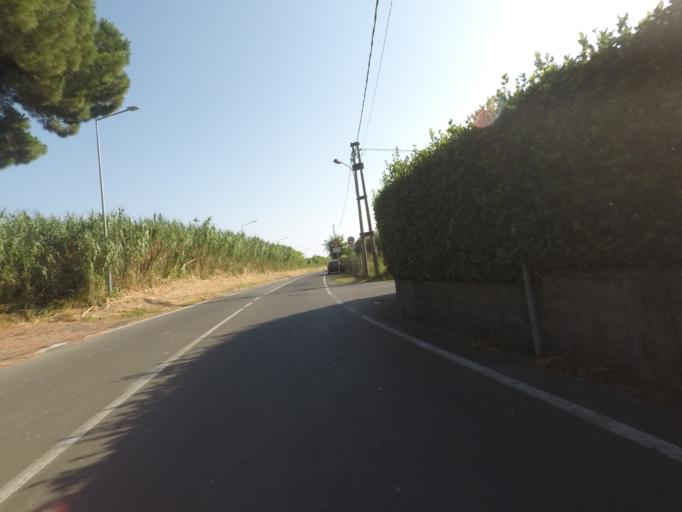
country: IT
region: Liguria
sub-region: Provincia di La Spezia
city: Casano-Dogana-Isola
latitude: 44.0628
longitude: 10.0307
